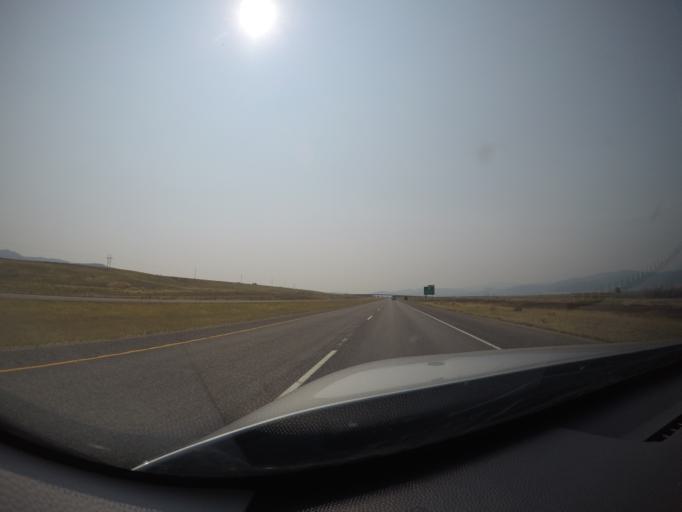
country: US
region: Montana
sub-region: Deer Lodge County
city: Warm Springs
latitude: 46.1142
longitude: -112.7994
